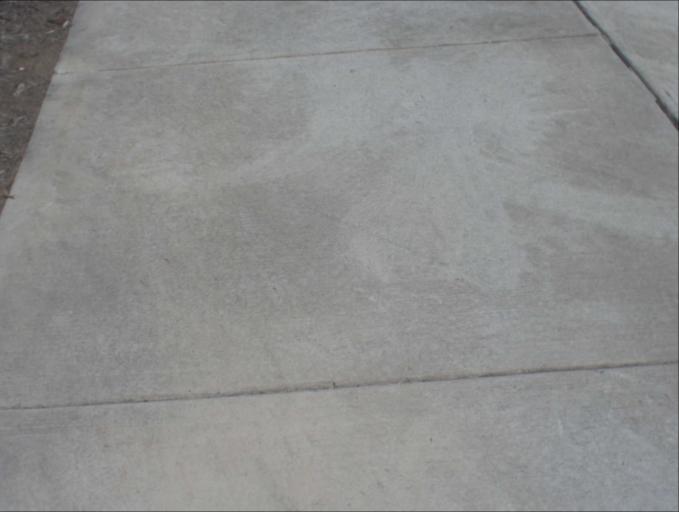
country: AU
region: Queensland
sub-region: Logan
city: Windaroo
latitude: -27.7177
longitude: 153.1663
